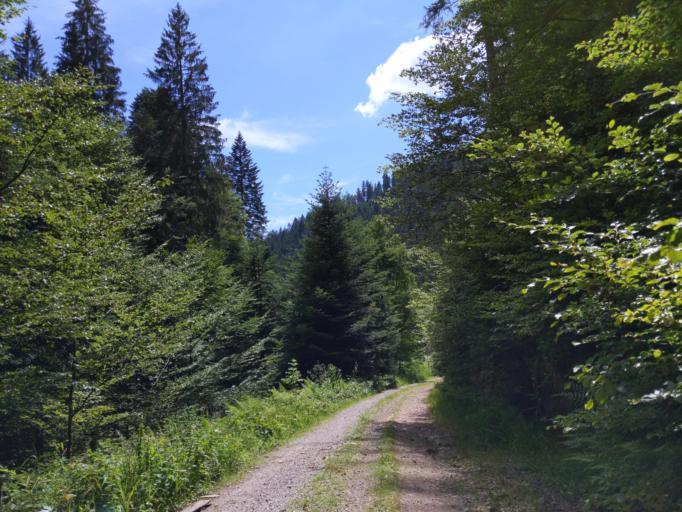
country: DE
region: Baden-Wuerttemberg
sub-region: Karlsruhe Region
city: Bad Rippoldsau-Schapbach
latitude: 48.4216
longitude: 8.3644
